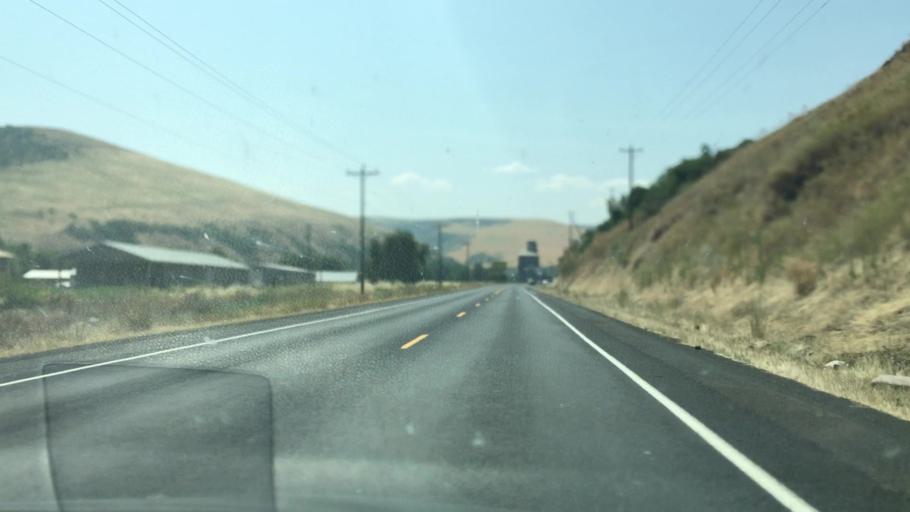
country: US
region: Idaho
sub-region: Nez Perce County
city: Lapwai
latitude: 46.3800
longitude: -116.7961
